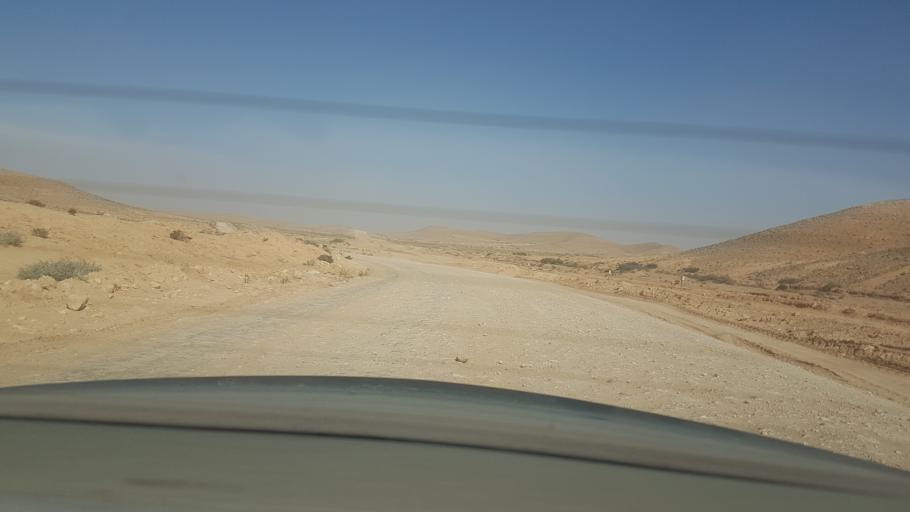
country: TN
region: Qabis
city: Matmata
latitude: 33.6402
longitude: 9.7367
